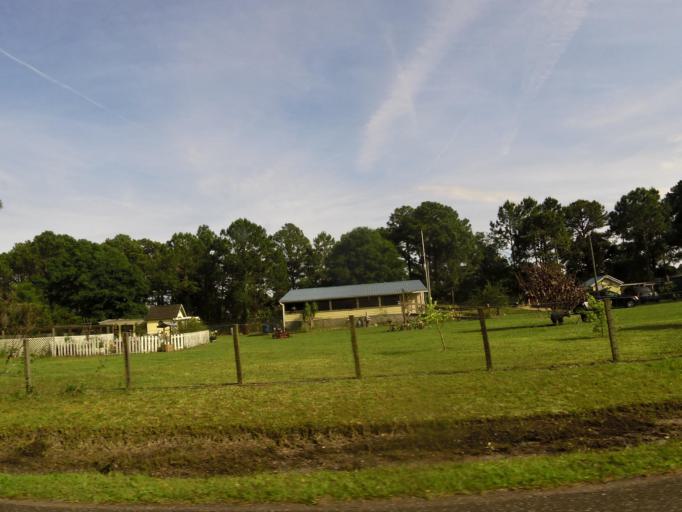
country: US
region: Florida
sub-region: Nassau County
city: Fernandina Beach
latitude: 30.5117
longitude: -81.4731
